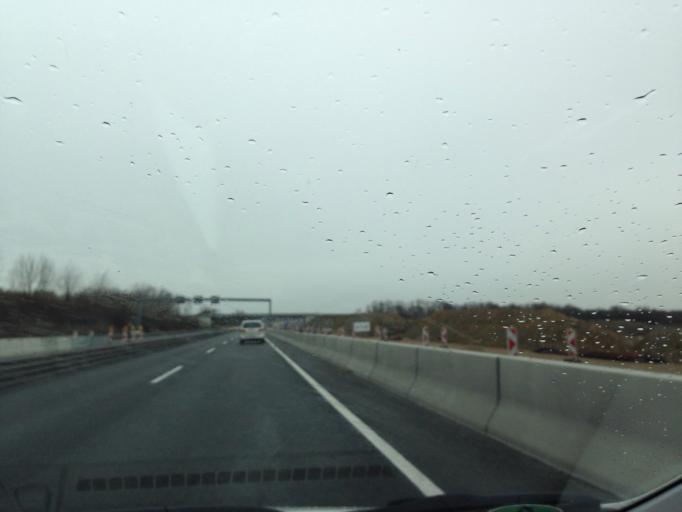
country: DE
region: North Rhine-Westphalia
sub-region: Regierungsbezirk Dusseldorf
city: Kaarst
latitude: 51.2375
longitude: 6.6378
